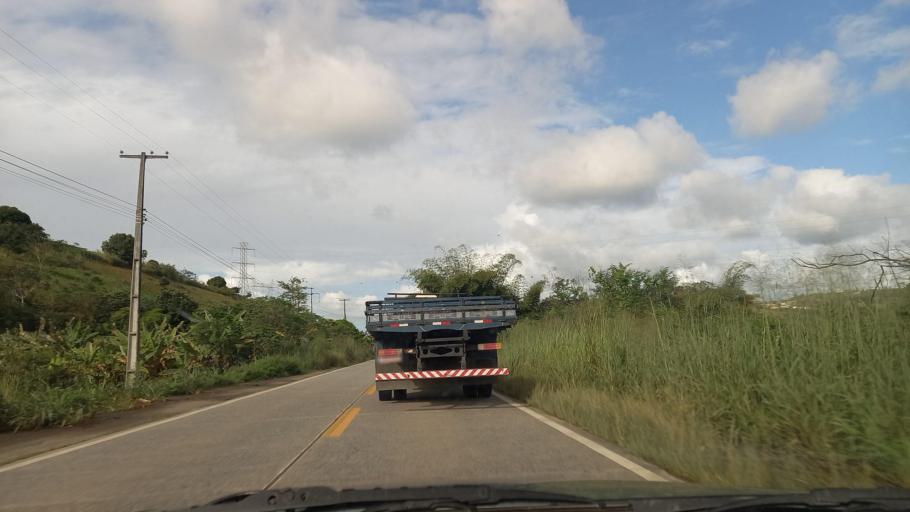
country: BR
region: Pernambuco
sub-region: Palmares
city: Palmares
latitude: -8.6913
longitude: -35.6187
